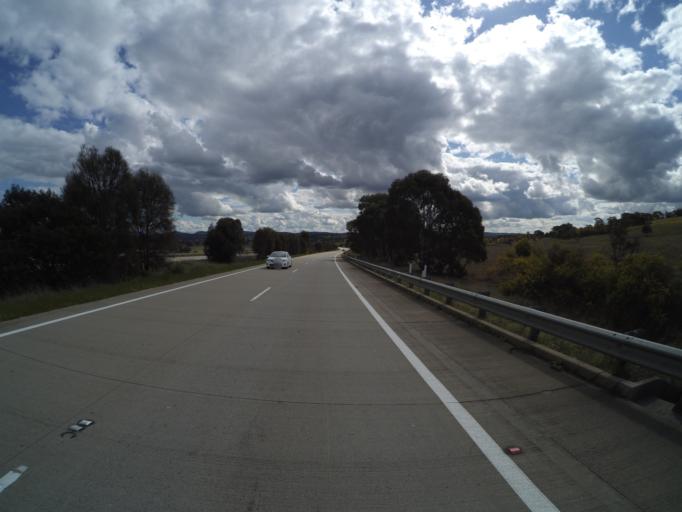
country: AU
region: New South Wales
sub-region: Yass Valley
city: Murrumbateman
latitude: -34.8012
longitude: 149.1489
